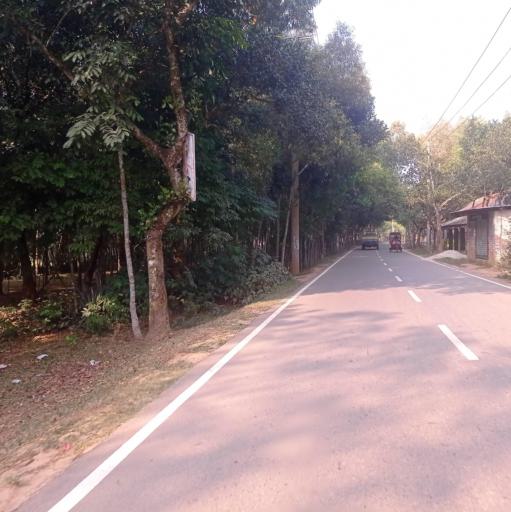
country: BD
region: Dhaka
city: Bhairab Bazar
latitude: 24.0683
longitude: 90.8416
